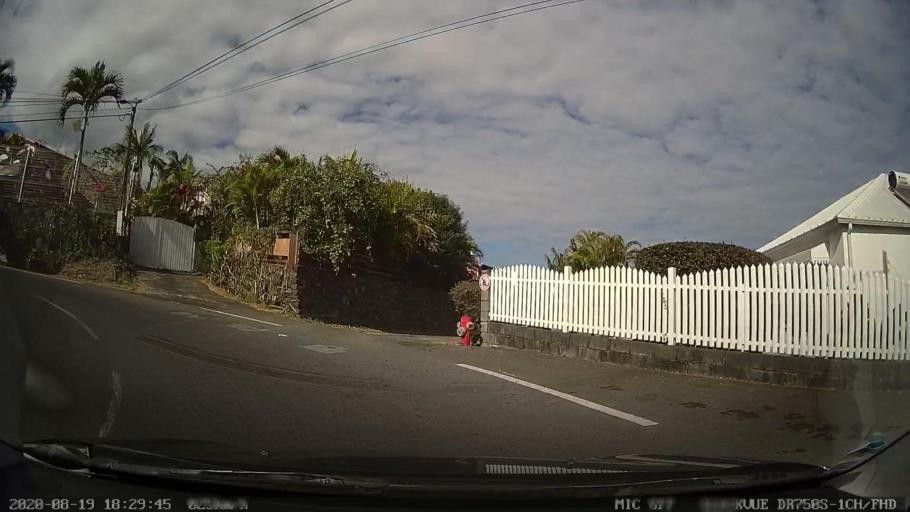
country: RE
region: Reunion
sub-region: Reunion
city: La Possession
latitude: -20.9588
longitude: 55.3482
